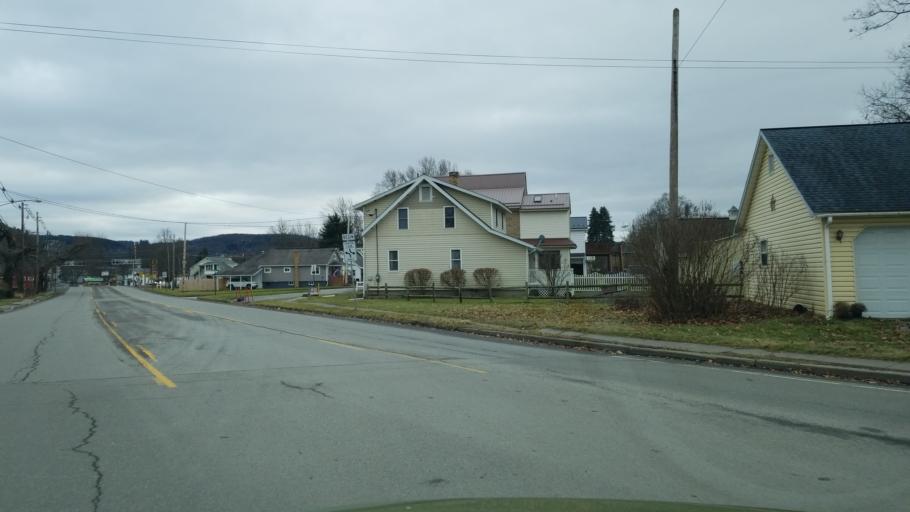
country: US
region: Pennsylvania
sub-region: Clearfield County
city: Clearfield
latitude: 41.0327
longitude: -78.4420
